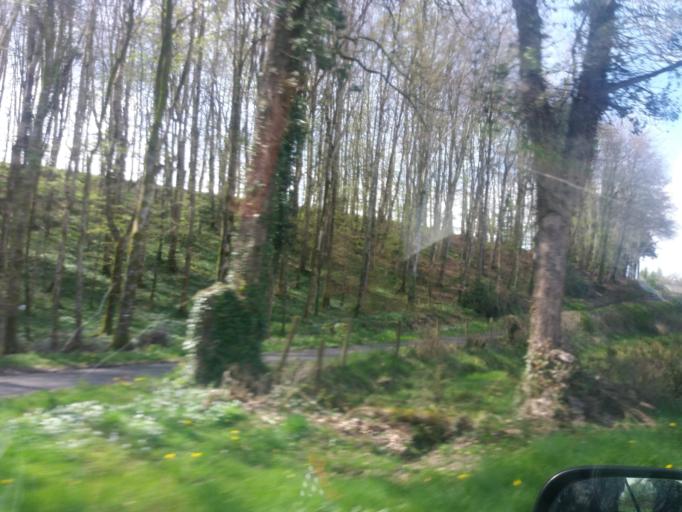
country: GB
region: Northern Ireland
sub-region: Fermanagh District
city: Enniskillen
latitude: 54.3876
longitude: -7.6977
